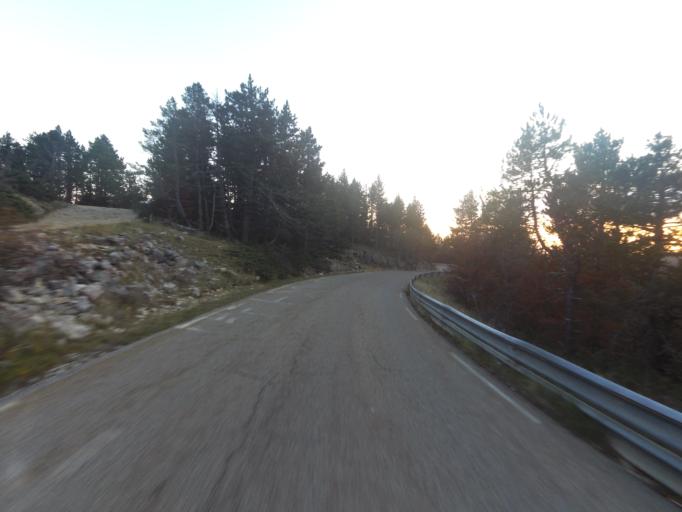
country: FR
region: Provence-Alpes-Cote d'Azur
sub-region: Departement du Vaucluse
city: Sault
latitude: 44.1478
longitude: 5.3161
